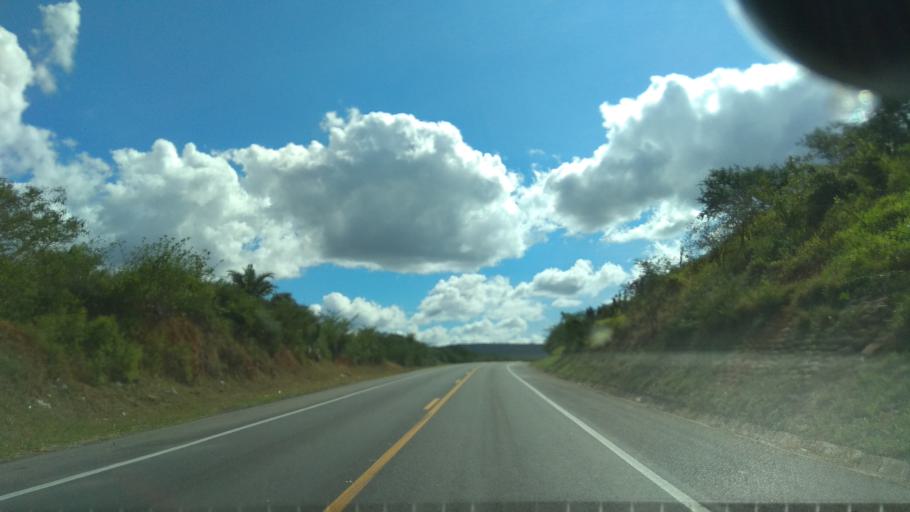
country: BR
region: Bahia
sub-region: Santa Ines
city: Santa Ines
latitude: -13.3107
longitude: -40.0230
